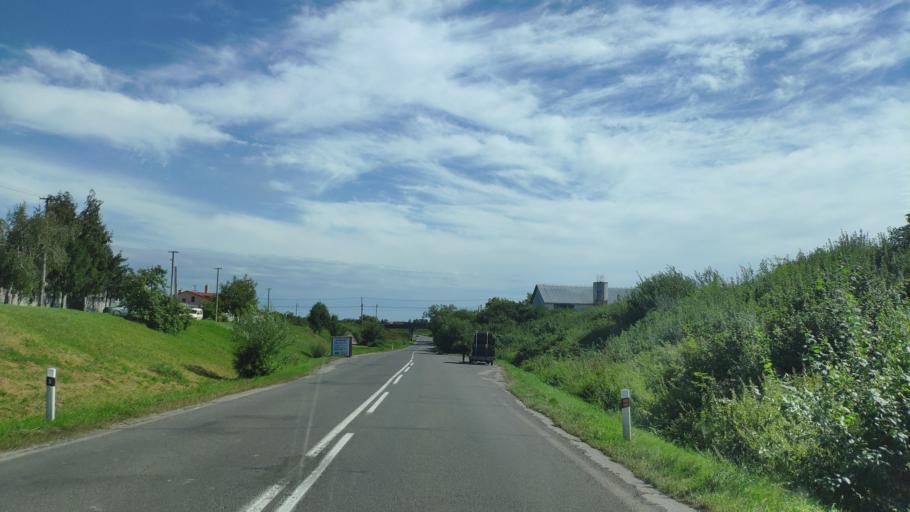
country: SK
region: Kosicky
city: Secovce
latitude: 48.6224
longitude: 21.5902
